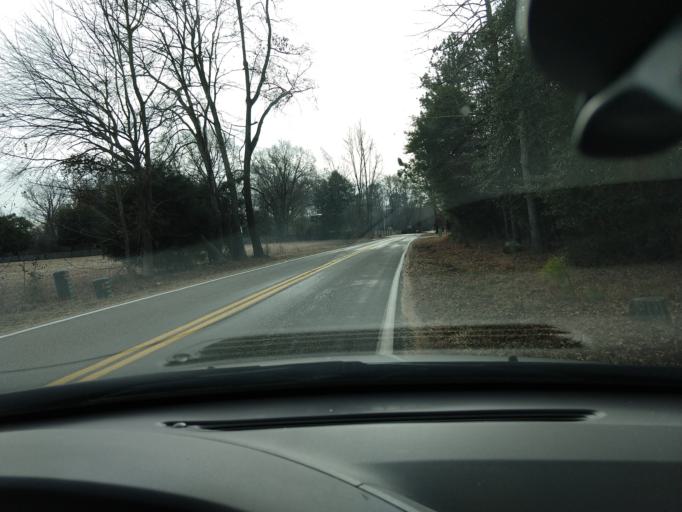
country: US
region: Virginia
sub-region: Henrico County
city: Fort Lee
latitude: 37.4375
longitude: -77.2351
